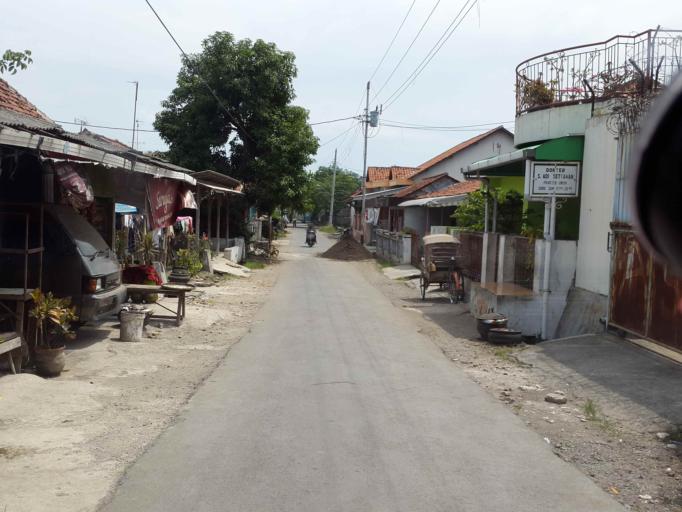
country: ID
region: Central Java
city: Pemalang
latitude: -6.8916
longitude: 109.3991
